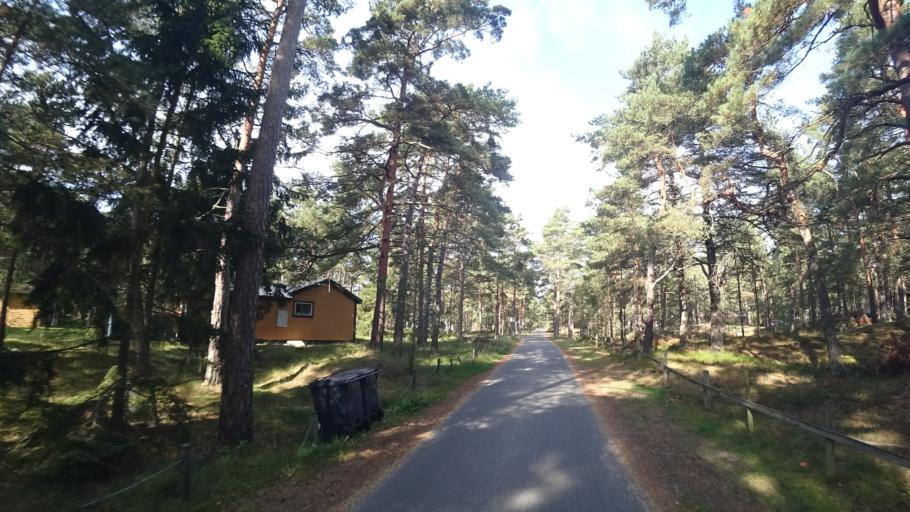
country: SE
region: Skane
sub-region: Kristianstads Kommun
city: Ahus
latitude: 55.9090
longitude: 14.2995
